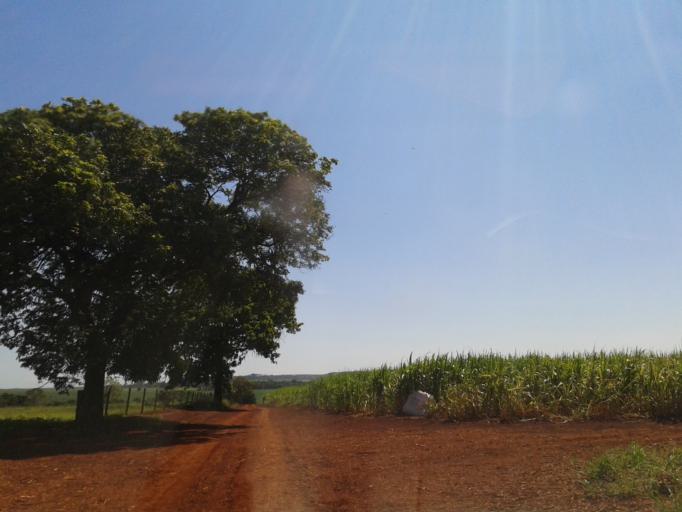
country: BR
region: Minas Gerais
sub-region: Centralina
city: Centralina
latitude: -18.6356
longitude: -49.2528
